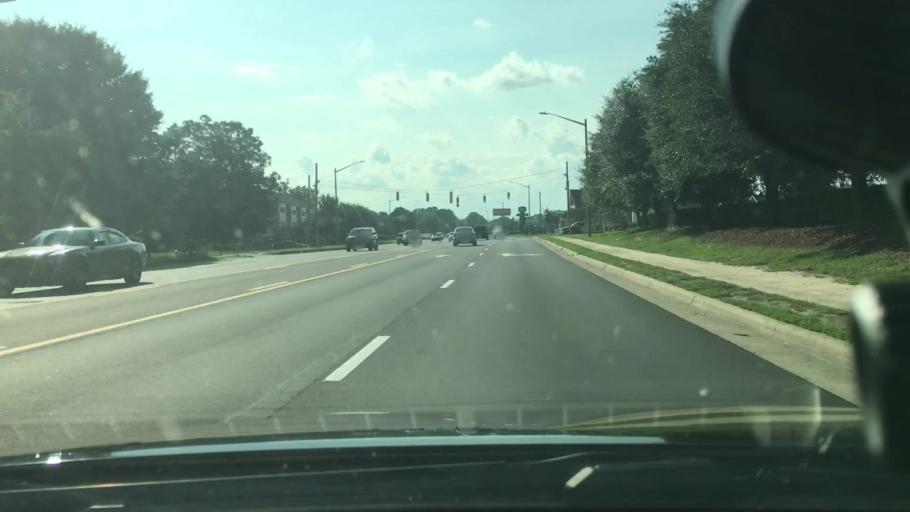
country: US
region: North Carolina
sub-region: Pitt County
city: Greenville
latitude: 35.5980
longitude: -77.3273
